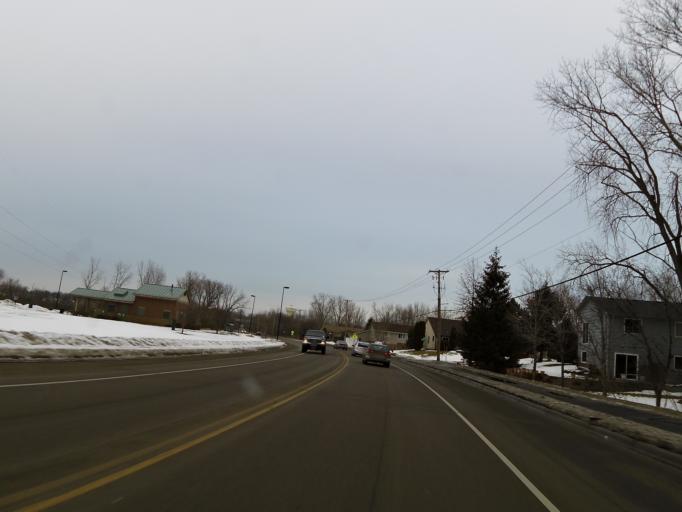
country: US
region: Minnesota
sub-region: Washington County
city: Oakdale
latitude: 44.9729
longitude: -92.9640
